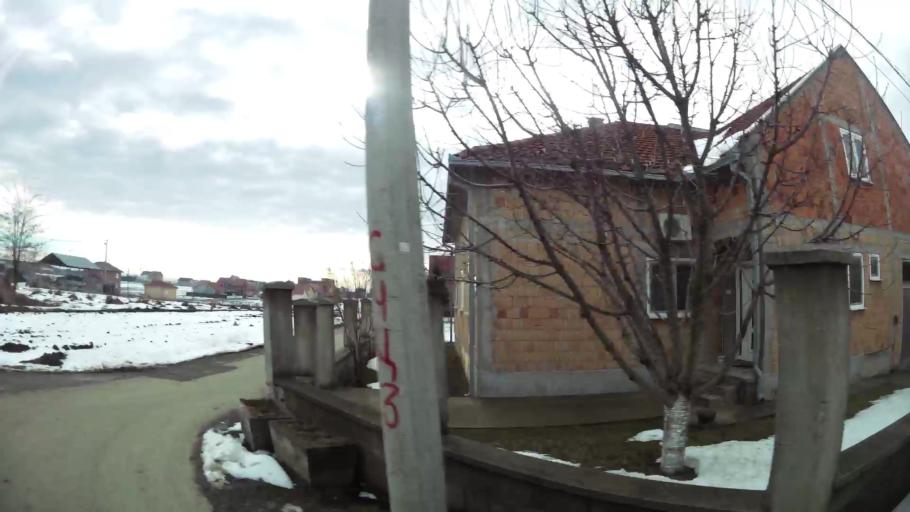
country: RS
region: Central Serbia
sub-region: Belgrade
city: Surcin
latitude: 44.7991
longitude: 20.2985
